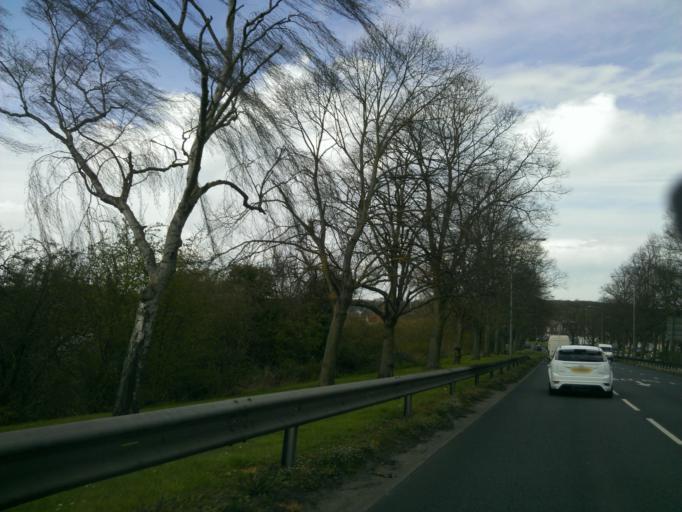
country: GB
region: England
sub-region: Essex
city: Colchester
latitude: 51.8940
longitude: 0.9160
